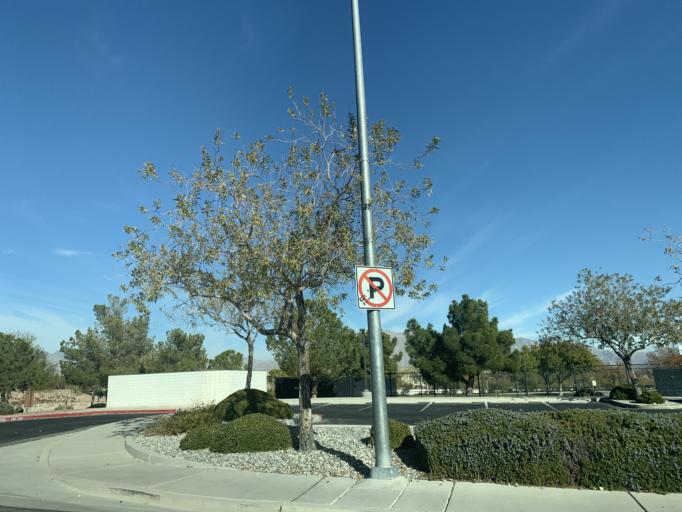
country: US
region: Nevada
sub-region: Clark County
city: Summerlin South
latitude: 36.3130
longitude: -115.2962
